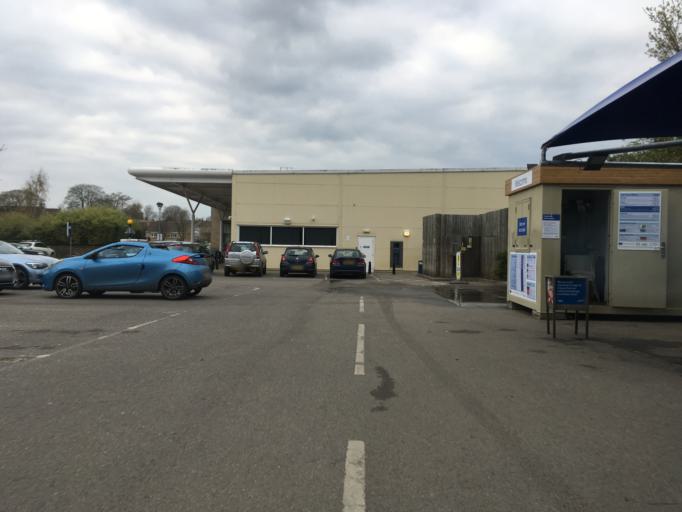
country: GB
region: England
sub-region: Gloucestershire
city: Tetbury
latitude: 51.6420
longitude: -2.1556
